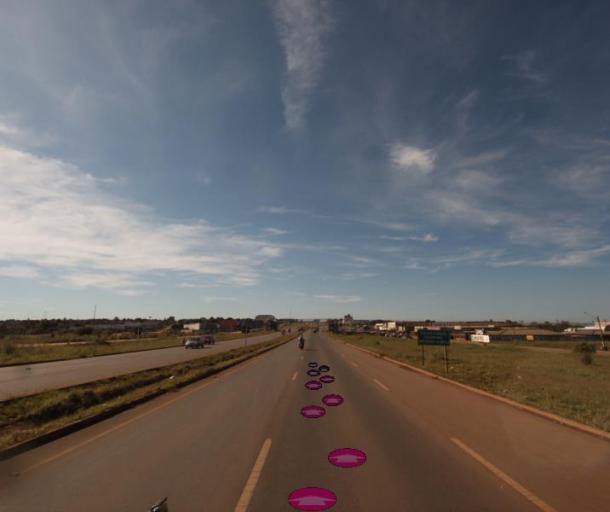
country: BR
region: Federal District
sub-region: Brasilia
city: Brasilia
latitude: -15.7389
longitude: -48.2727
